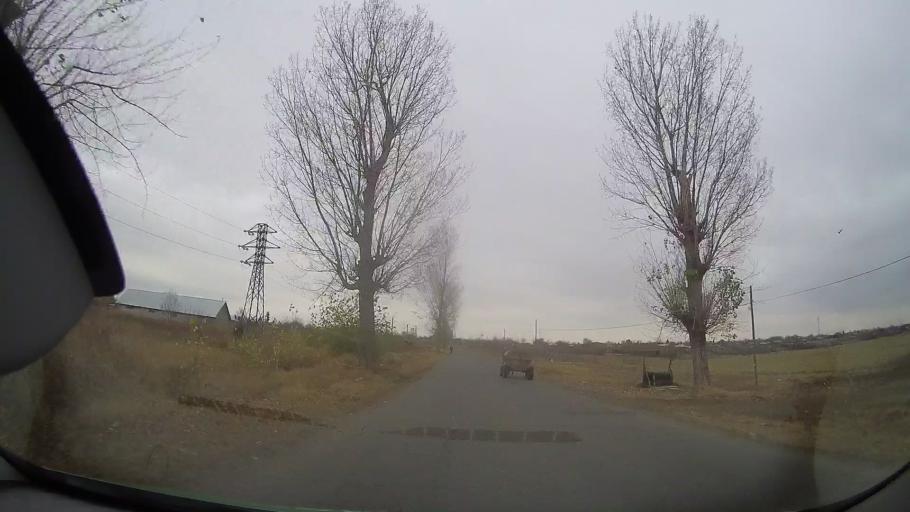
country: RO
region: Buzau
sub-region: Comuna Rusetu
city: Rusetu
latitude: 44.9519
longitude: 27.2217
